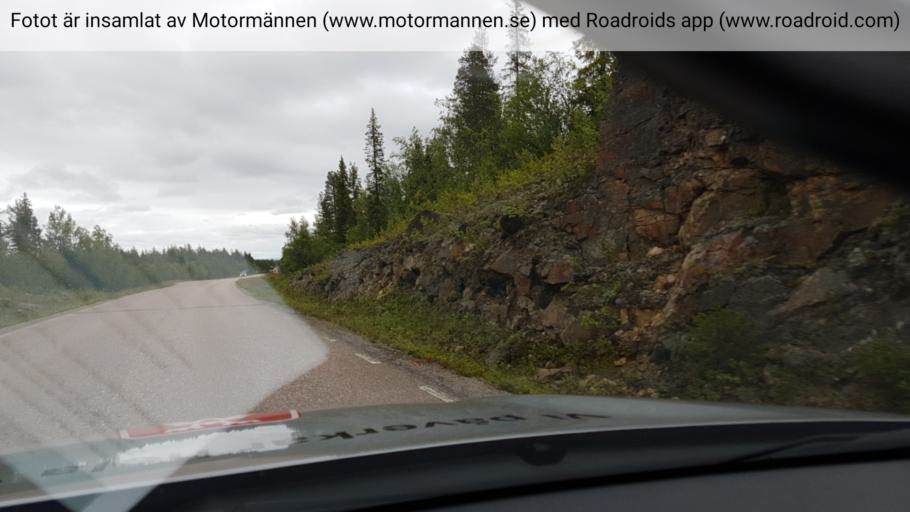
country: SE
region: Norrbotten
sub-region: Overkalix Kommun
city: OEverkalix
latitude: 67.0451
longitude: 22.0631
